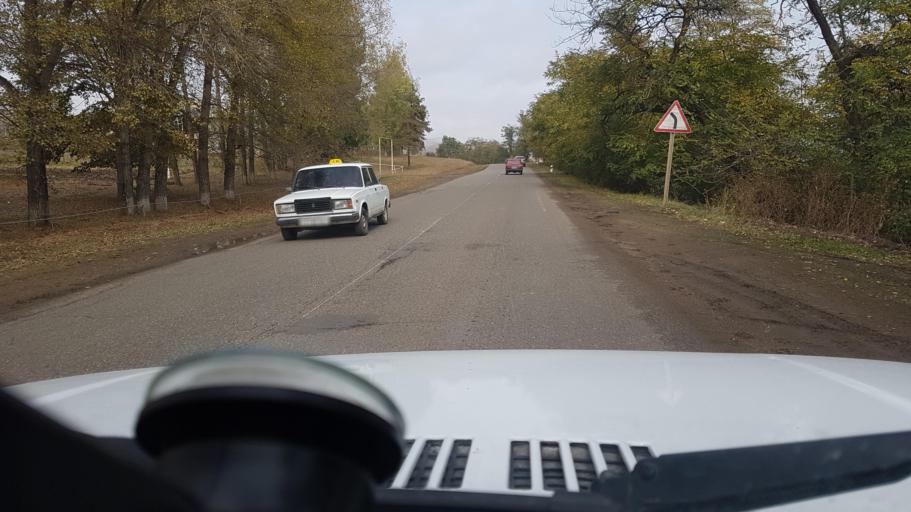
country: AZ
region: Gadabay Rayon
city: Ariqdam
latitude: 40.6439
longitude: 45.8128
